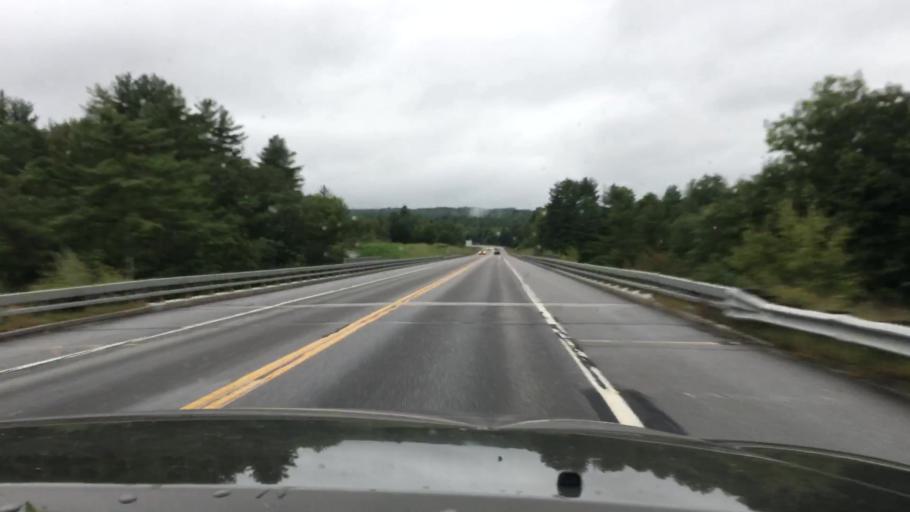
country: US
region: New Hampshire
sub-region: Hillsborough County
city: Hillsborough
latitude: 43.1171
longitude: -71.9284
